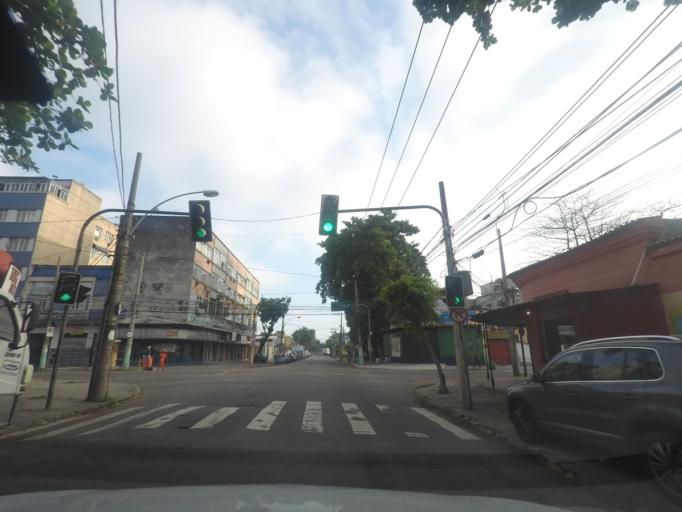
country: BR
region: Rio de Janeiro
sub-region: Duque De Caxias
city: Duque de Caxias
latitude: -22.8367
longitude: -43.2789
